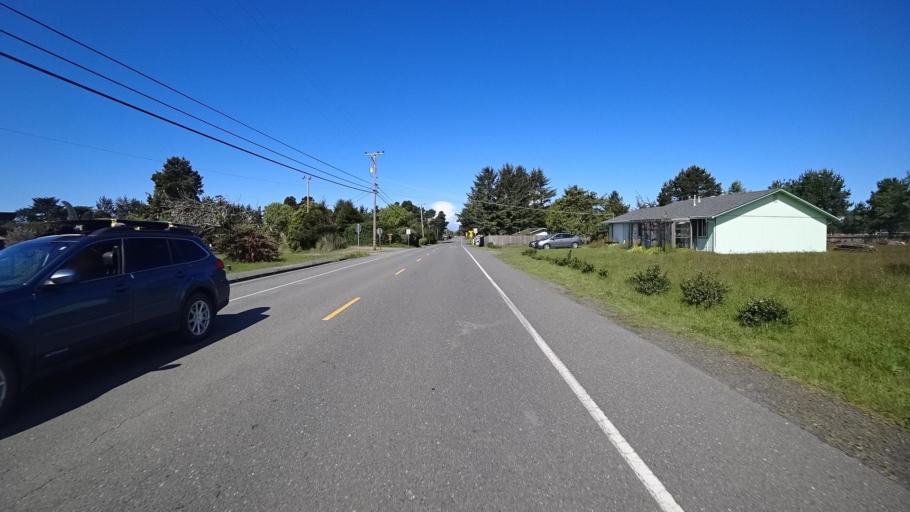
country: US
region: California
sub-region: Humboldt County
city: McKinleyville
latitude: 40.9417
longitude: -124.1179
